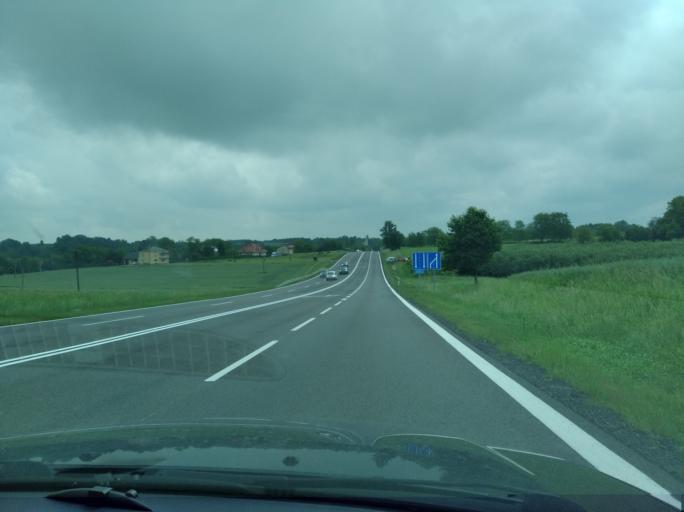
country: PL
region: Subcarpathian Voivodeship
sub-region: Powiat przeworski
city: Rozborz
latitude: 50.0460
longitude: 22.5429
